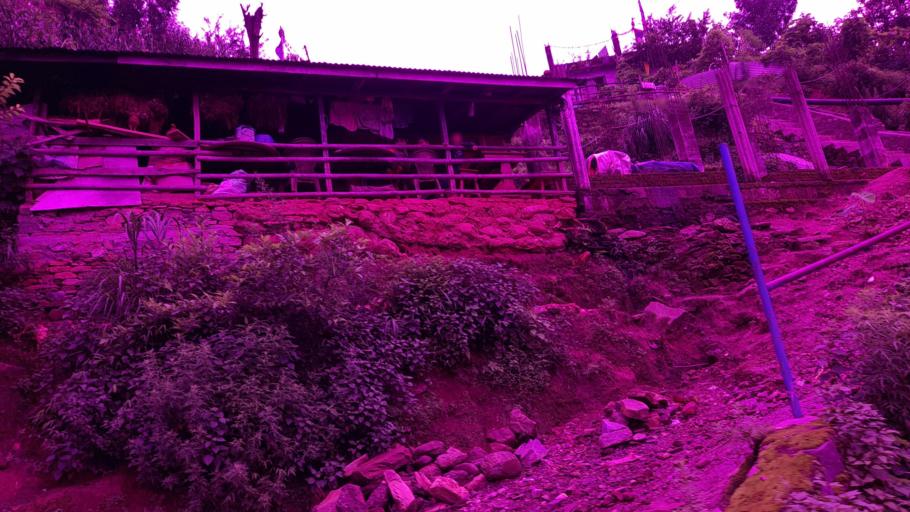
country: NP
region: Central Region
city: Kirtipur
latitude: 27.8167
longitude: 85.2136
